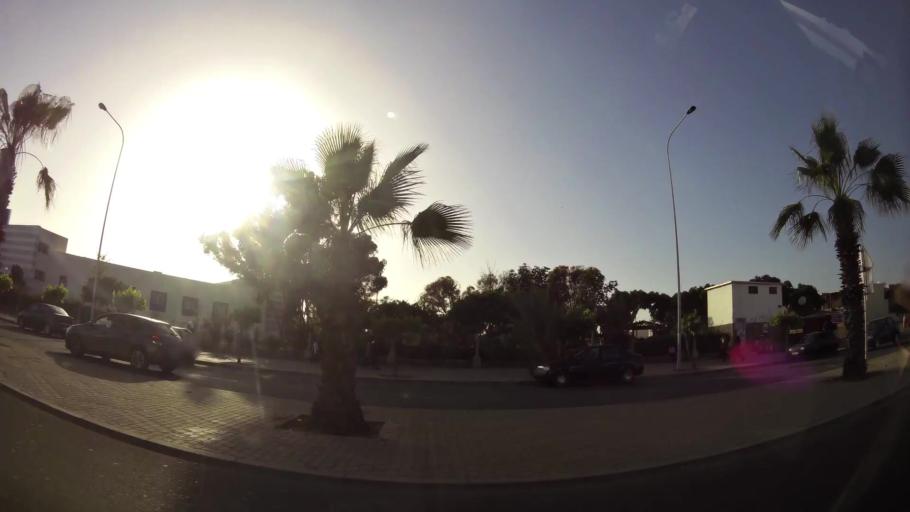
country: MA
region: Oued ed Dahab-Lagouira
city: Dakhla
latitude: 30.4073
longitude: -9.5504
